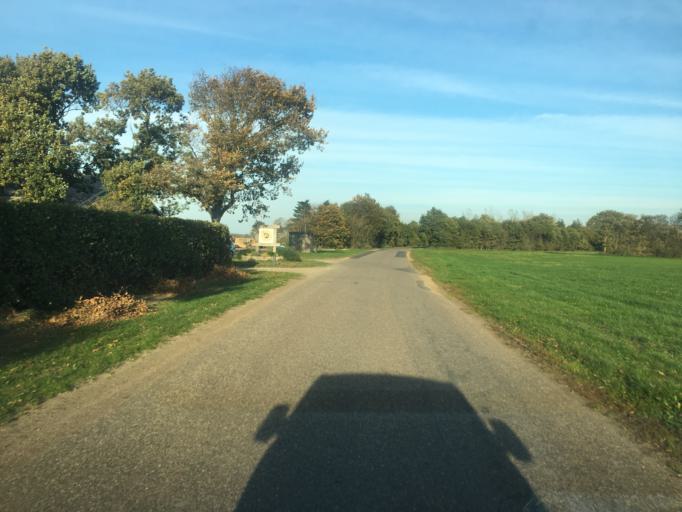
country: DE
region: Schleswig-Holstein
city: Ellhoft
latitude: 54.9150
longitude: 8.9443
